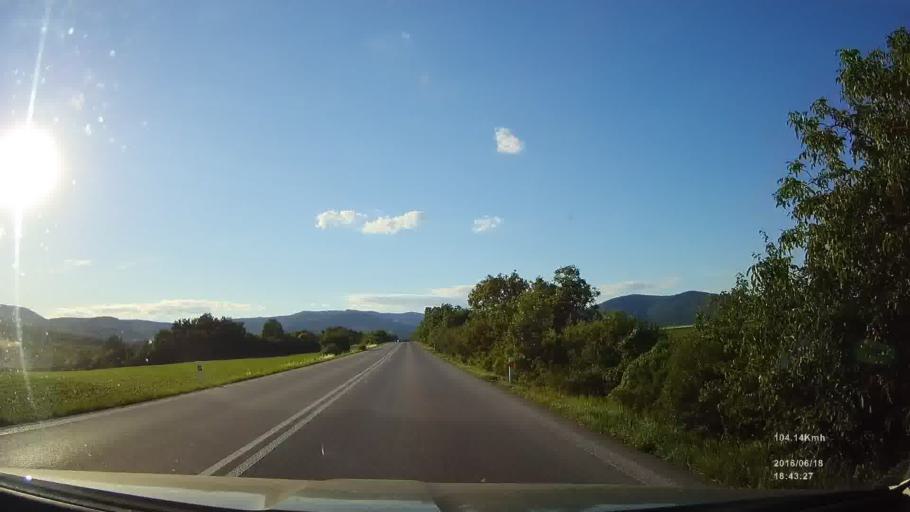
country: SK
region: Kosicky
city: Secovce
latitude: 48.7187
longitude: 21.6115
